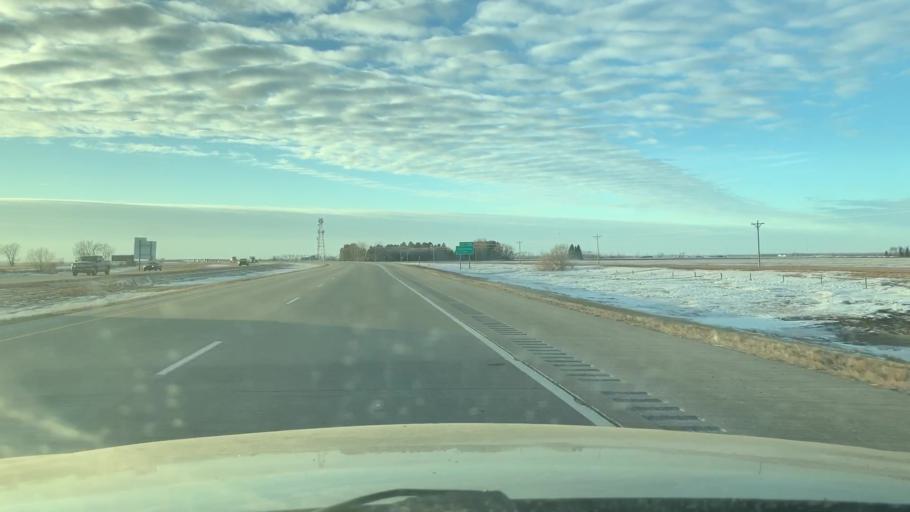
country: US
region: North Dakota
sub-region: Cass County
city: Casselton
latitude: 46.8756
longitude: -97.2345
